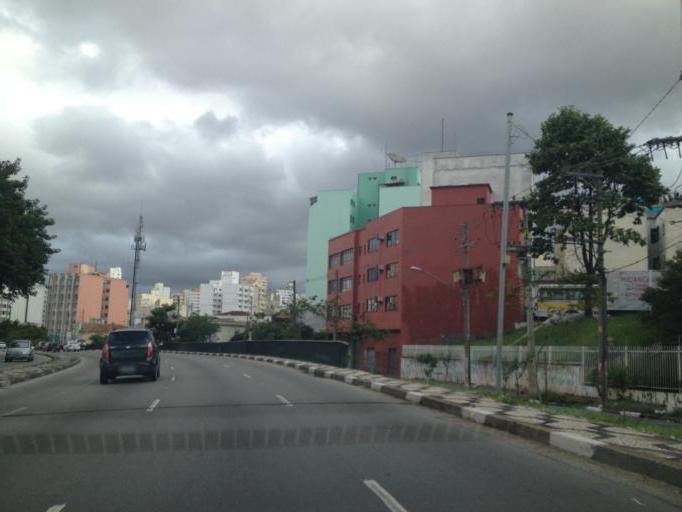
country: BR
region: Sao Paulo
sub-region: Sao Paulo
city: Sao Paulo
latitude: -23.5539
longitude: -46.6453
